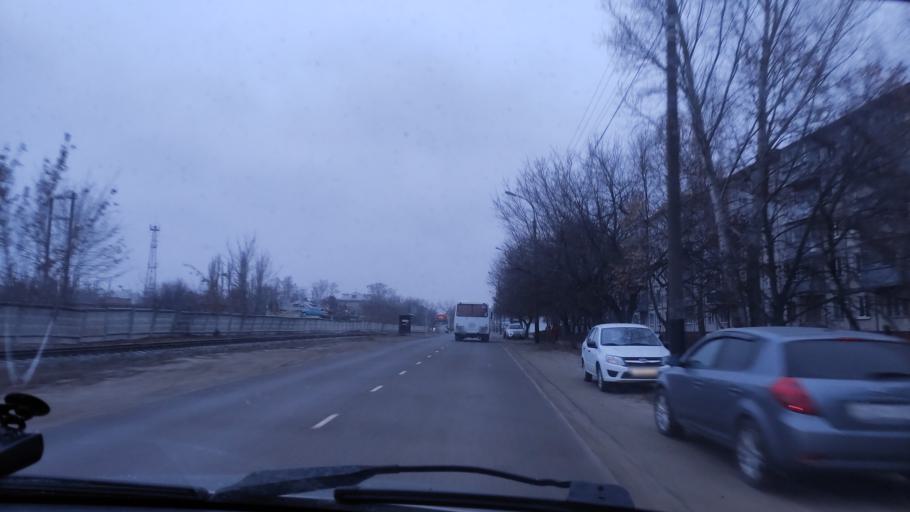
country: RU
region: Tambov
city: Pokrovo-Prigorodnoye
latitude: 52.7181
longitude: 41.3876
